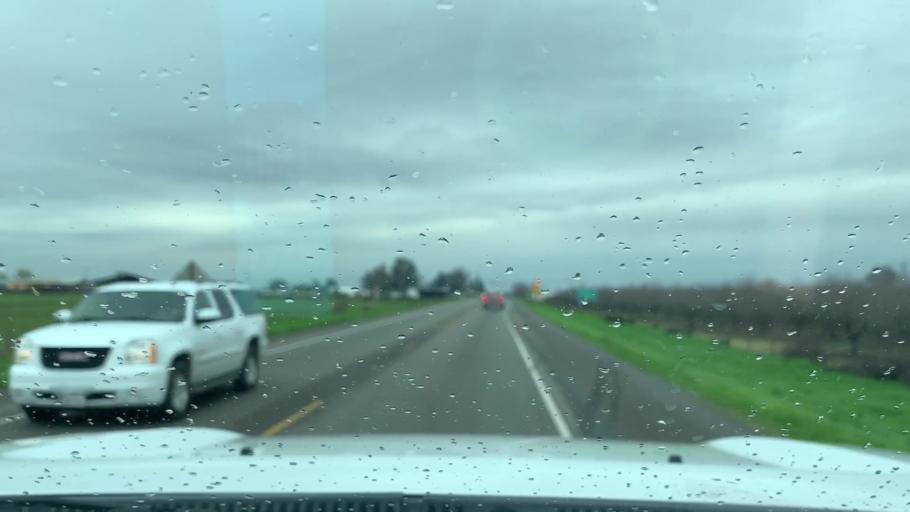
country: US
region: California
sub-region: Fresno County
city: Riverdale
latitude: 36.4275
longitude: -119.8019
